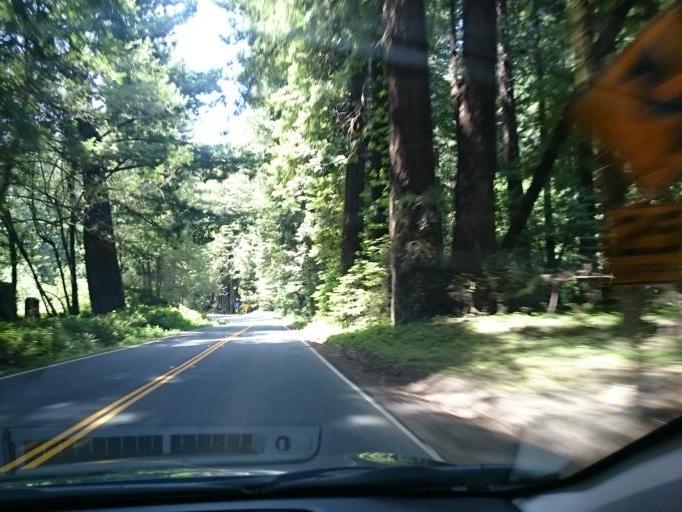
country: US
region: California
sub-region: Mendocino County
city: Boonville
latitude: 39.1554
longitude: -123.6171
